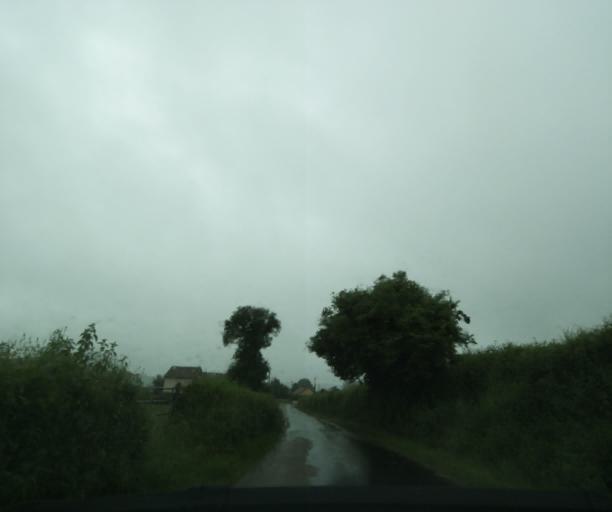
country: FR
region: Bourgogne
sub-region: Departement de Saone-et-Loire
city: Charolles
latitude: 46.4154
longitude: 4.2761
